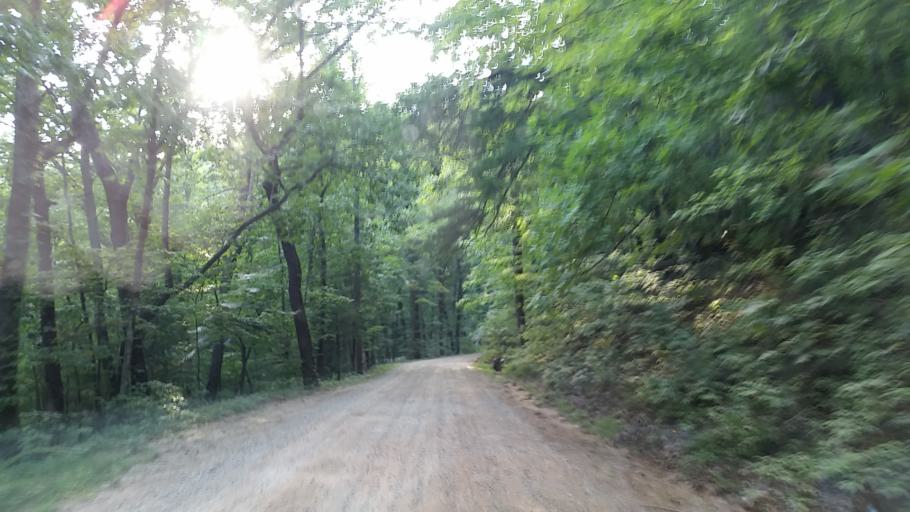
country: US
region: Georgia
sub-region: Lumpkin County
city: Dahlonega
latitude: 34.6395
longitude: -84.0963
